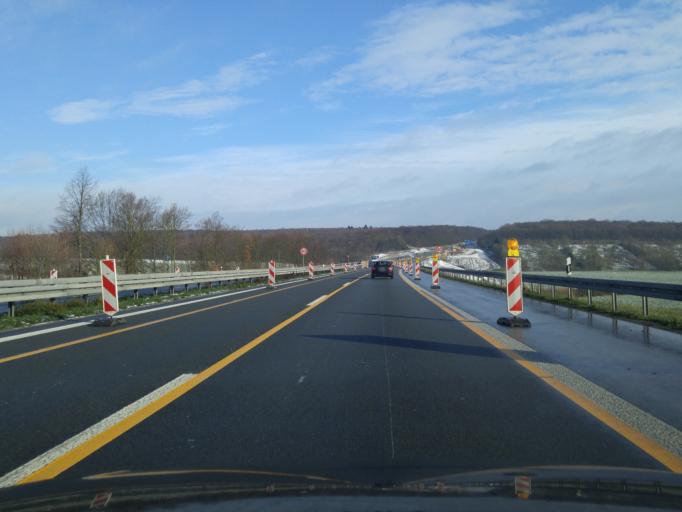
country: DE
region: Bavaria
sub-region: Regierungsbezirk Unterfranken
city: Werneck
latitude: 49.9835
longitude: 10.0473
